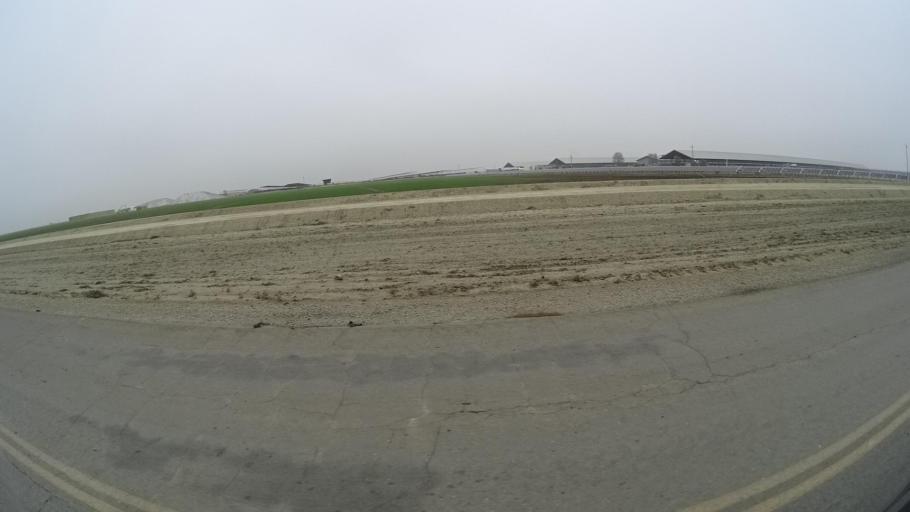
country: US
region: California
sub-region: Kern County
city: Rosedale
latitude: 35.2098
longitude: -119.2151
